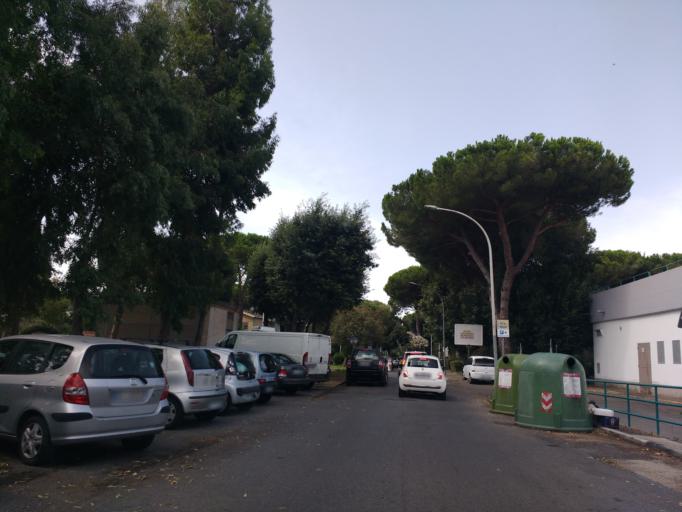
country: IT
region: Latium
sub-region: Citta metropolitana di Roma Capitale
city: Acilia-Castel Fusano-Ostia Antica
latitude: 41.7503
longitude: 12.3545
